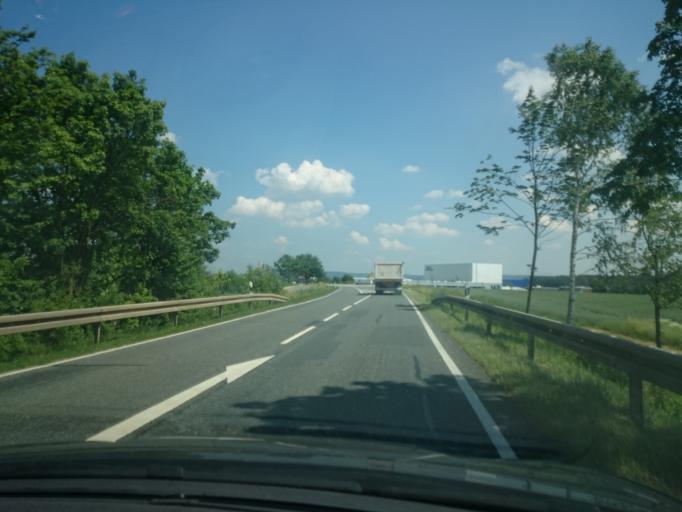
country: DE
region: Bavaria
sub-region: Regierungsbezirk Mittelfranken
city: Hilpoltstein
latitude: 49.1620
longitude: 11.2519
